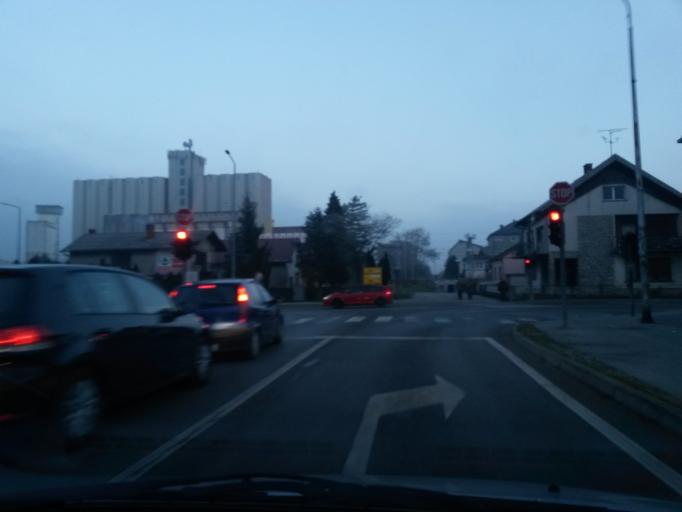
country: HR
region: Koprivnicko-Krizevacka
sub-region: Grad Koprivnica
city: Koprivnica
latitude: 46.1686
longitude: 16.8174
